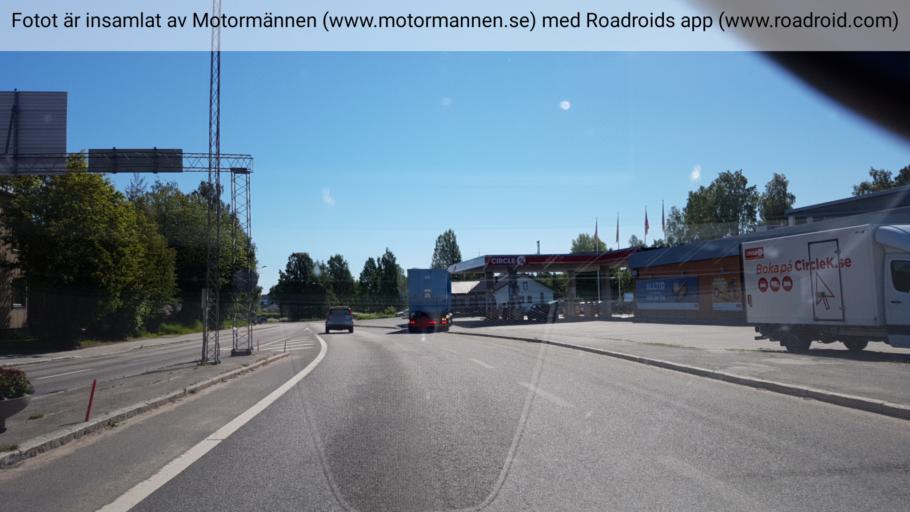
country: SE
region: Norrbotten
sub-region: Bodens Kommun
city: Boden
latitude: 65.8218
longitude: 21.6803
